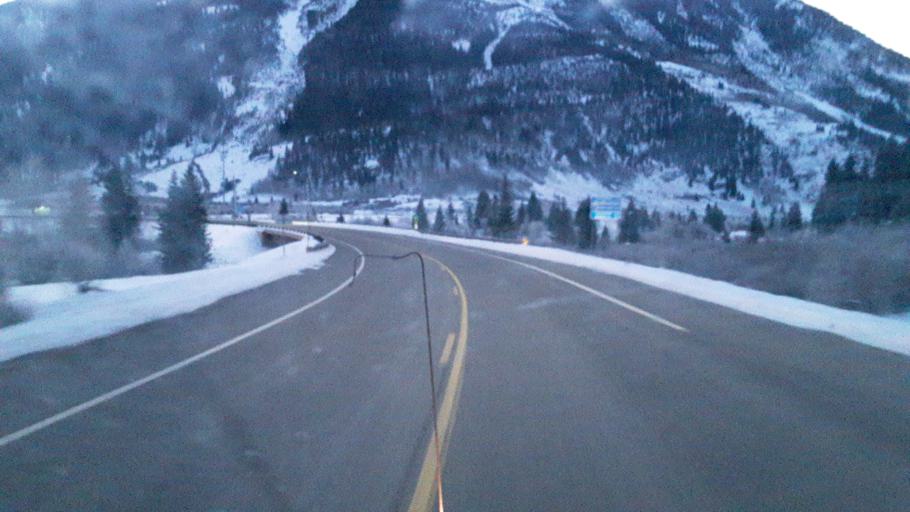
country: US
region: Colorado
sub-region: San Juan County
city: Silverton
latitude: 37.8037
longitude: -107.6743
